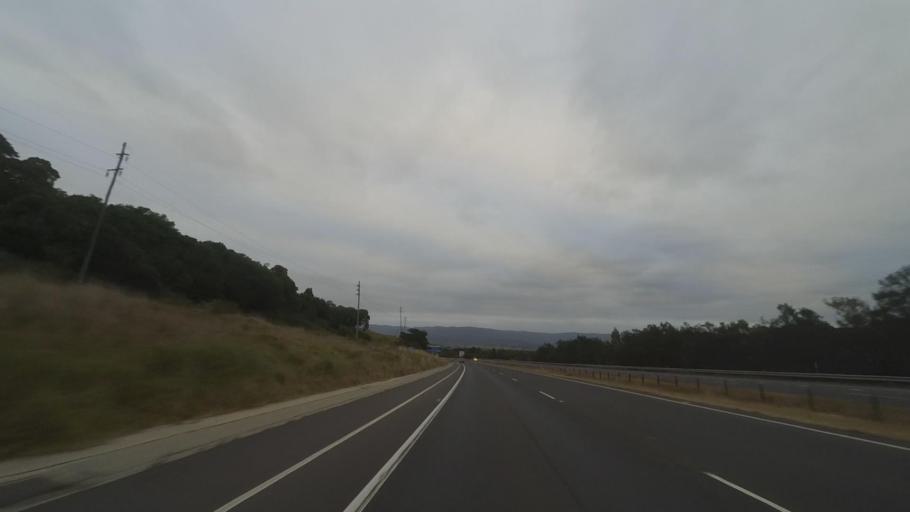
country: AU
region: New South Wales
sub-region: Shellharbour
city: Croom
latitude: -34.5762
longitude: 150.8299
